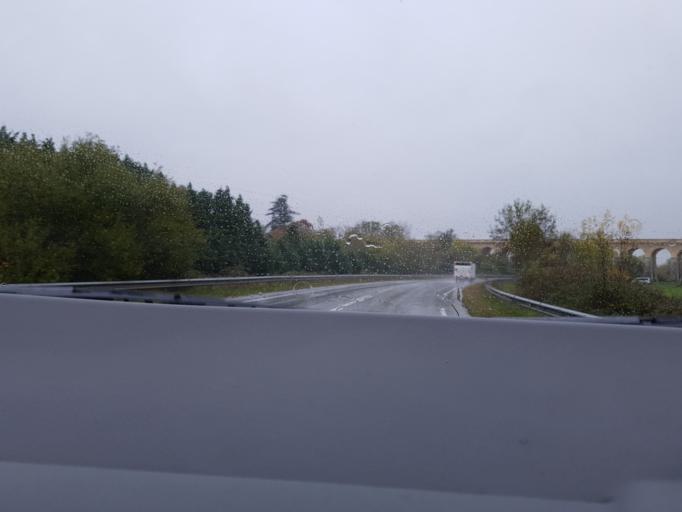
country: FR
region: Aquitaine
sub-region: Departement de la Gironde
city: Saint-Vincent-de-Paul
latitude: 44.9609
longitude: -0.4685
